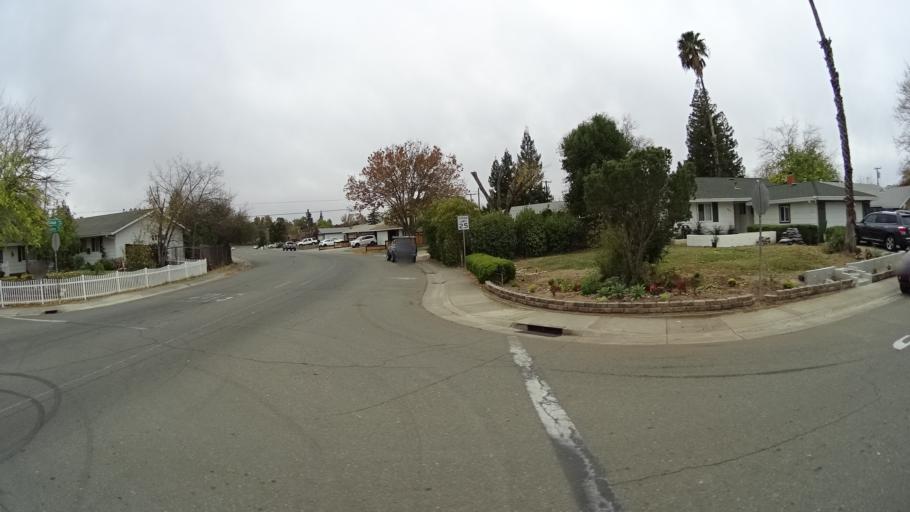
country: US
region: California
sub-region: Sacramento County
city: Antelope
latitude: 38.6922
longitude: -121.3059
